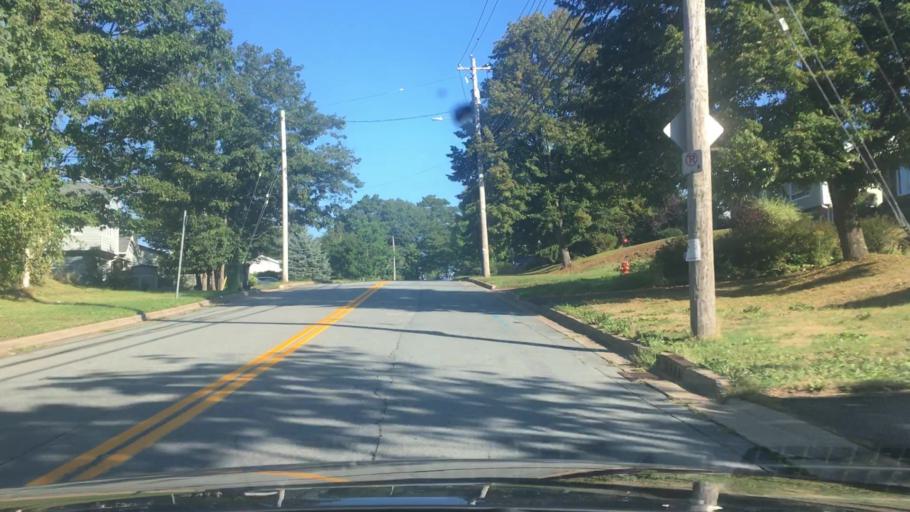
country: CA
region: Nova Scotia
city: Dartmouth
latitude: 44.7398
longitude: -63.6526
